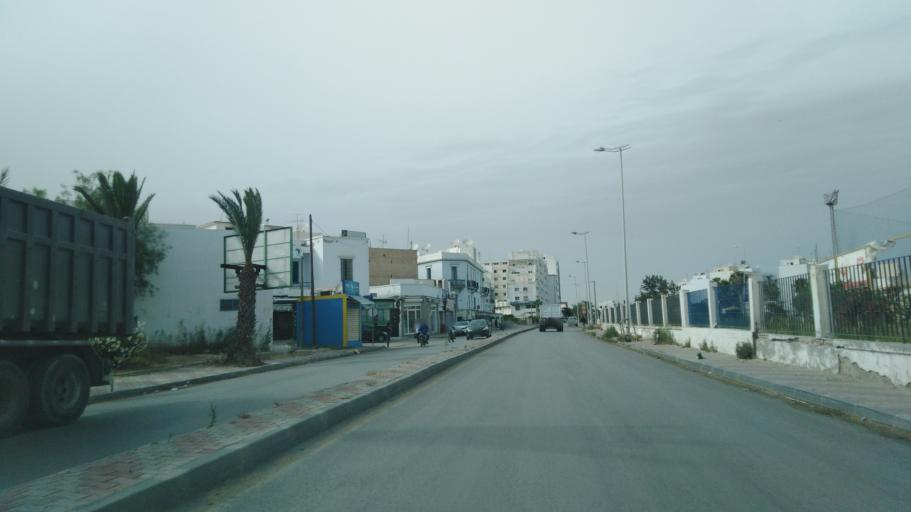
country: TN
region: Safaqis
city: Sfax
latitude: 34.7407
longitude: 10.7637
